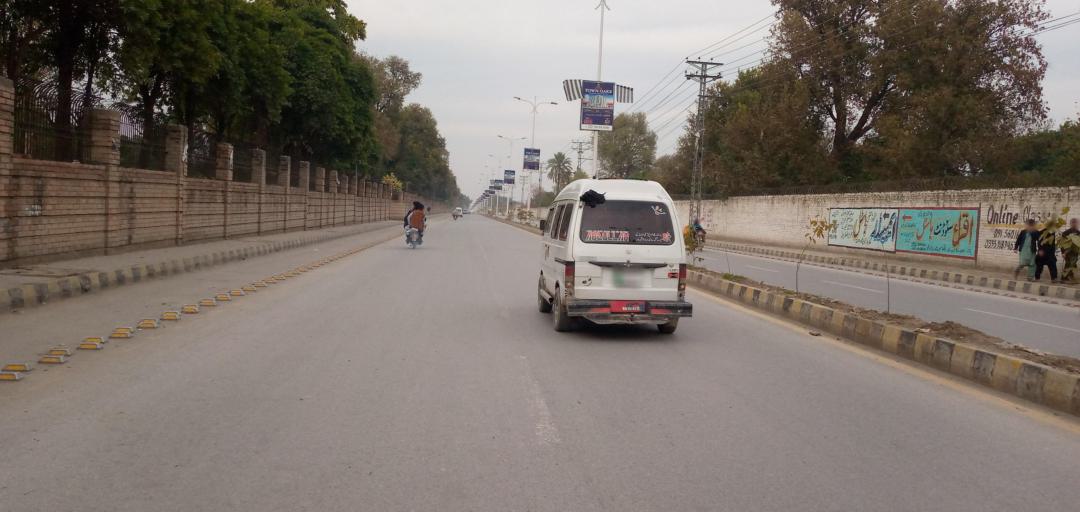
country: PK
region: Khyber Pakhtunkhwa
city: Peshawar
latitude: 33.9999
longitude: 71.4885
